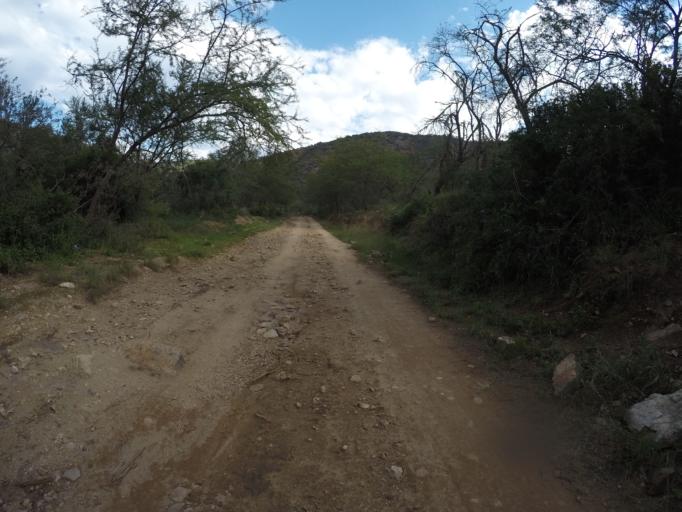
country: ZA
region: Eastern Cape
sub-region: Cacadu District Municipality
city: Kareedouw
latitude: -33.6366
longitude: 24.3171
